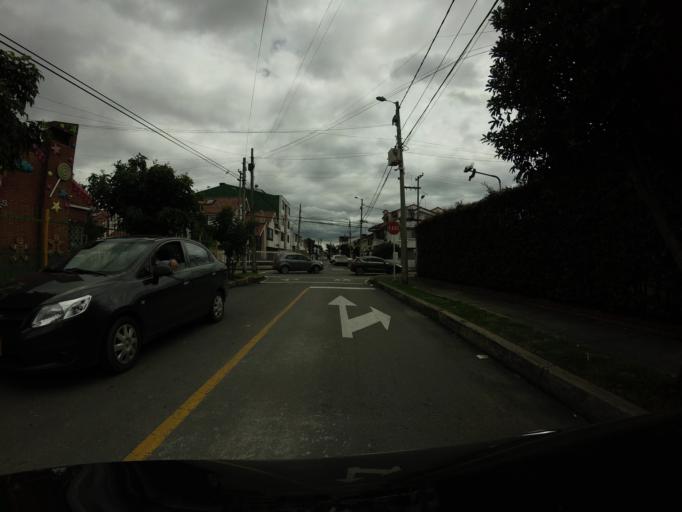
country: CO
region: Bogota D.C.
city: Barrio San Luis
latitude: 4.6990
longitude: -74.0594
